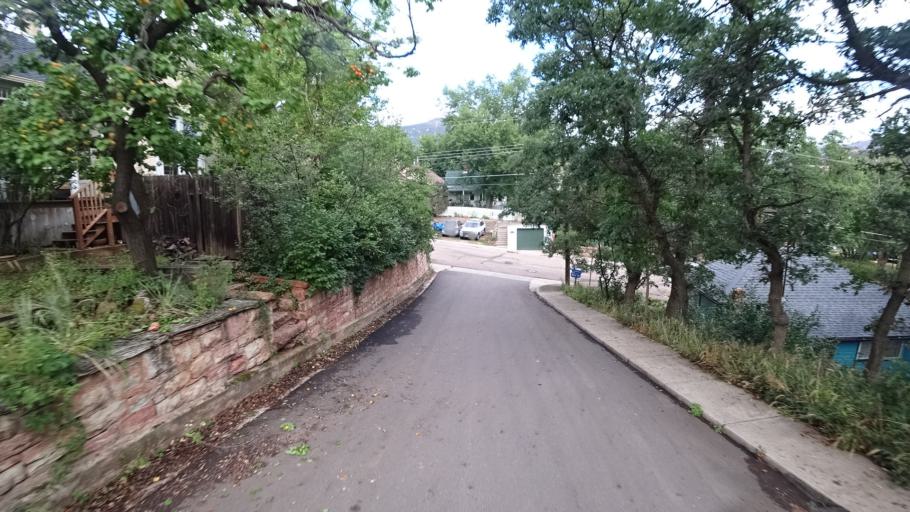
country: US
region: Colorado
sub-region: El Paso County
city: Manitou Springs
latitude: 38.8562
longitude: -104.9123
